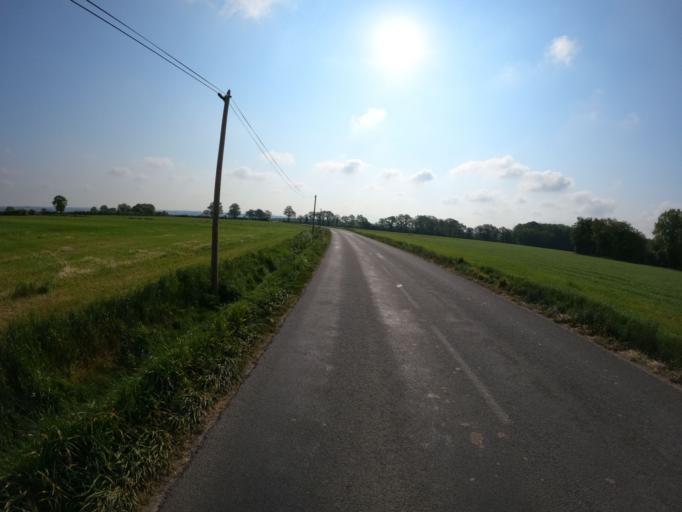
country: FR
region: Pays de la Loire
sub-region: Departement de Maine-et-Loire
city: La Romagne
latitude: 47.0645
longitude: -1.0408
